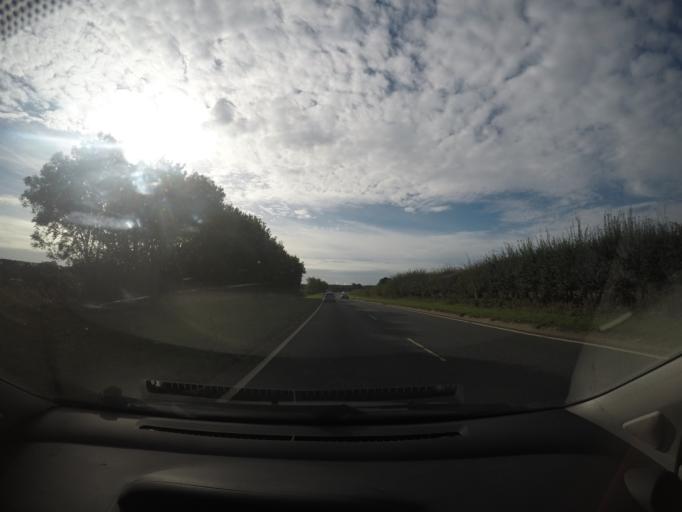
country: GB
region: England
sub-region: North Yorkshire
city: Riccall
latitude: 53.8611
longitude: -1.0508
